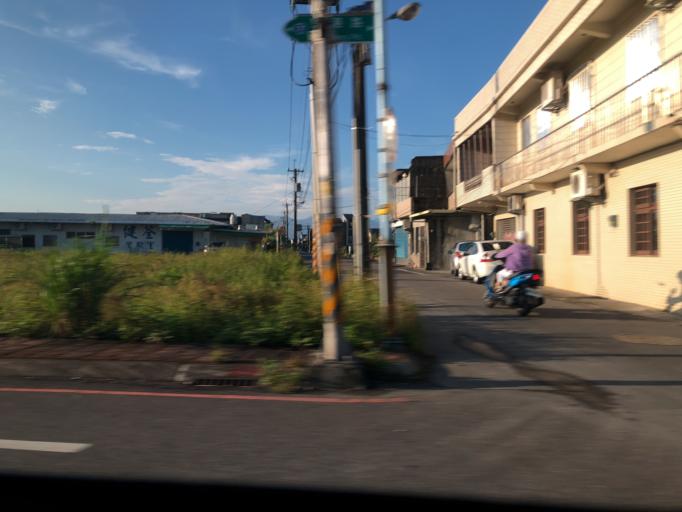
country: TW
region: Taiwan
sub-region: Yilan
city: Yilan
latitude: 24.7501
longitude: 121.7735
